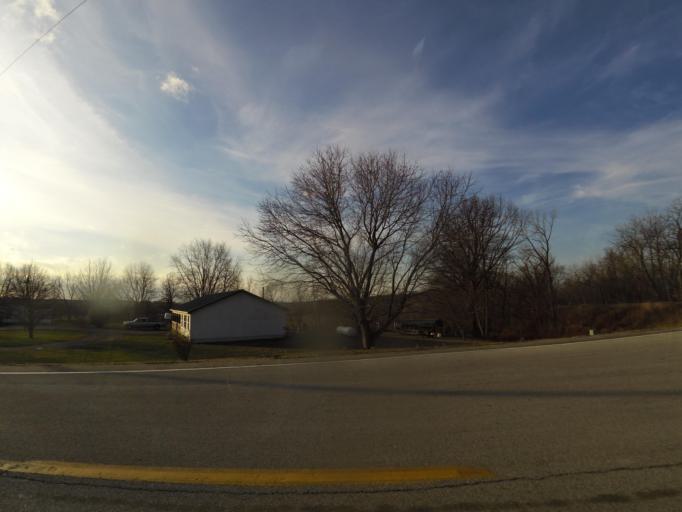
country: US
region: Illinois
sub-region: Bond County
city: Greenville
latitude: 38.9230
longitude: -89.2528
